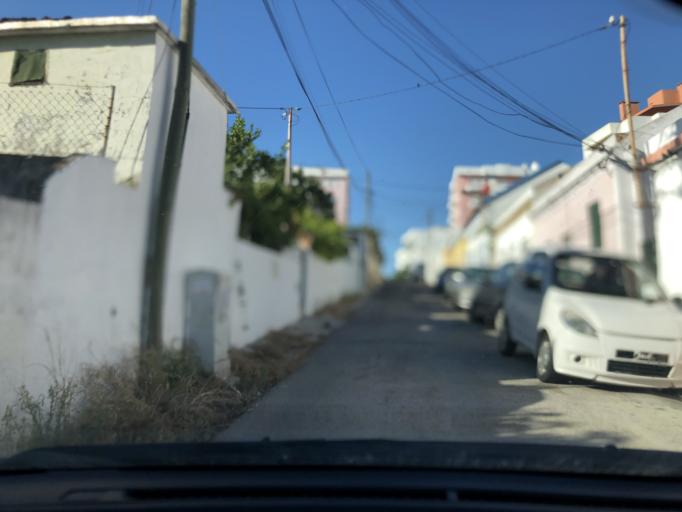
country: PT
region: Setubal
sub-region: Setubal
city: Setubal
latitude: 38.5405
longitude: -8.8776
